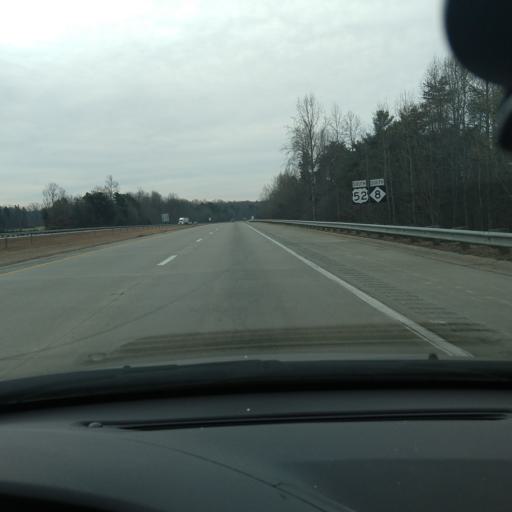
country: US
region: North Carolina
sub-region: Davidson County
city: Midway
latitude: 35.9343
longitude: -80.2328
